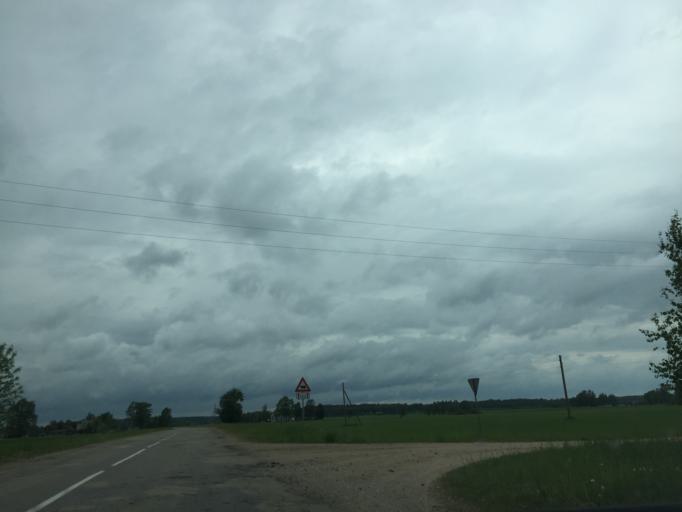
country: LV
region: Varkava
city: Vecvarkava
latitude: 56.1007
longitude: 26.5224
